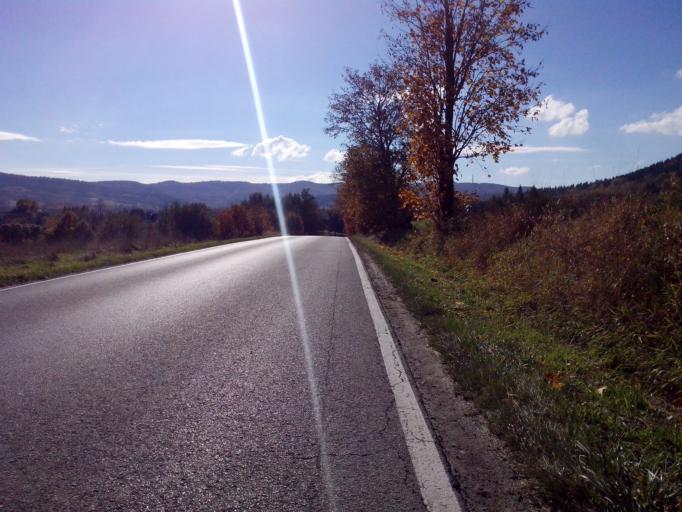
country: PL
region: Subcarpathian Voivodeship
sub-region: Powiat strzyzowski
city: Jawornik
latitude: 49.7953
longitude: 21.8604
